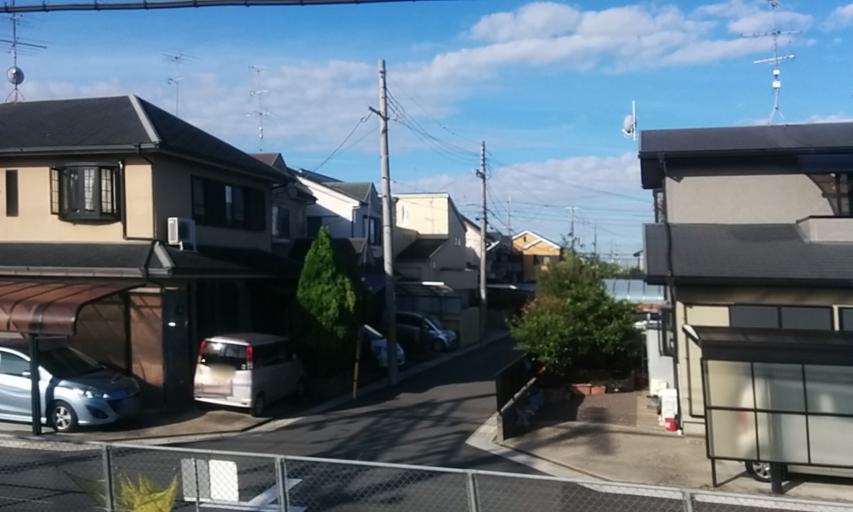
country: JP
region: Kyoto
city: Tanabe
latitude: 34.8505
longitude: 135.7717
